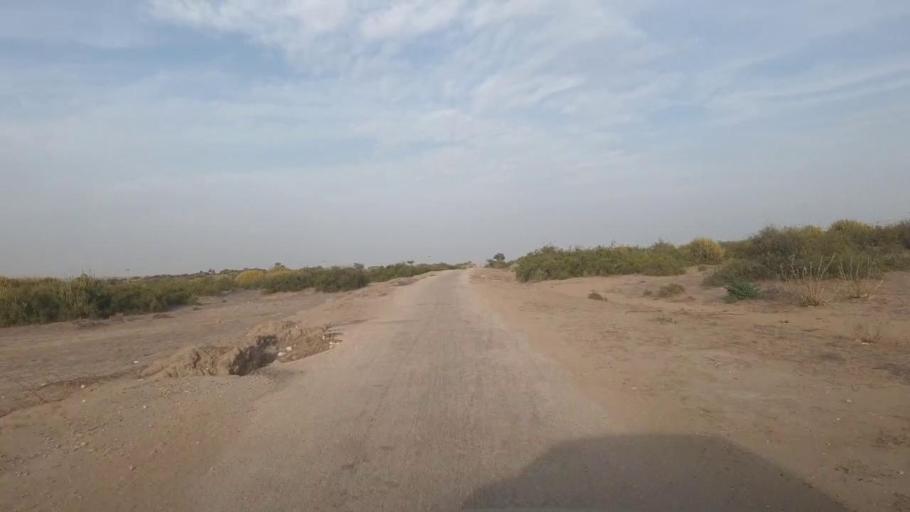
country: PK
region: Sindh
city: Nabisar
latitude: 25.0981
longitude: 69.6588
